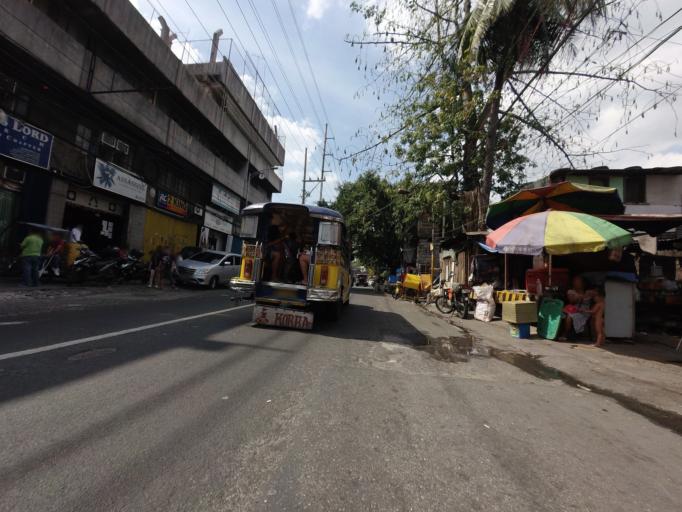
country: PH
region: Metro Manila
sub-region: City of Manila
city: Quiapo
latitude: 14.5724
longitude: 120.9984
